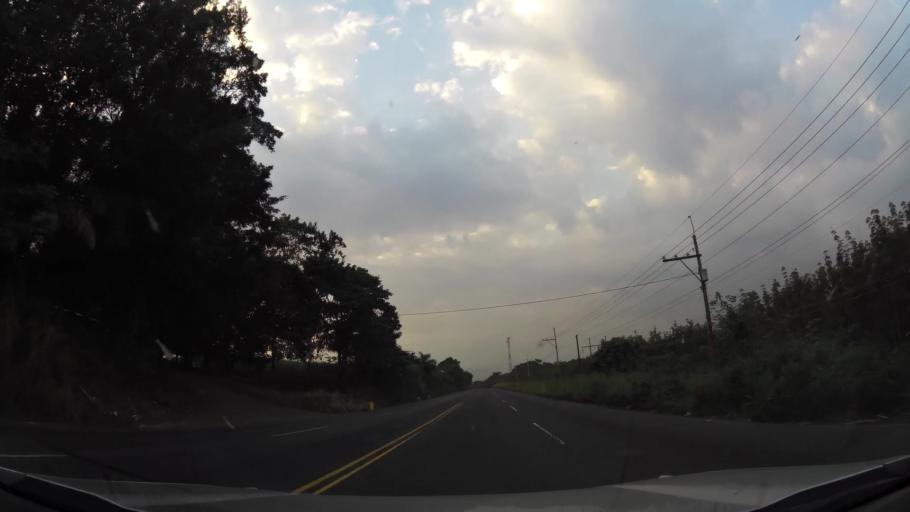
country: GT
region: Escuintla
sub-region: Municipio de La Democracia
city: La Democracia
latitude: 14.2723
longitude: -90.9067
